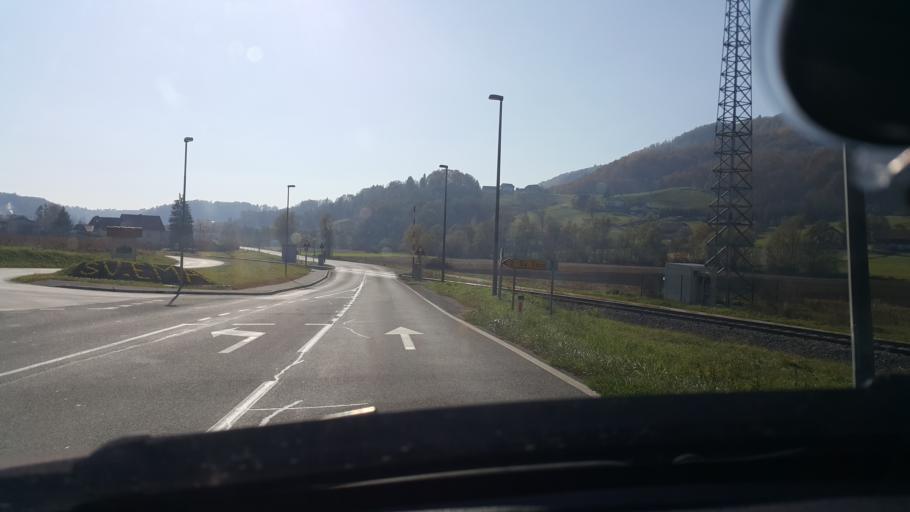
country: SI
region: Podcetrtek
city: Podcetrtek
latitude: 46.1789
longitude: 15.6003
